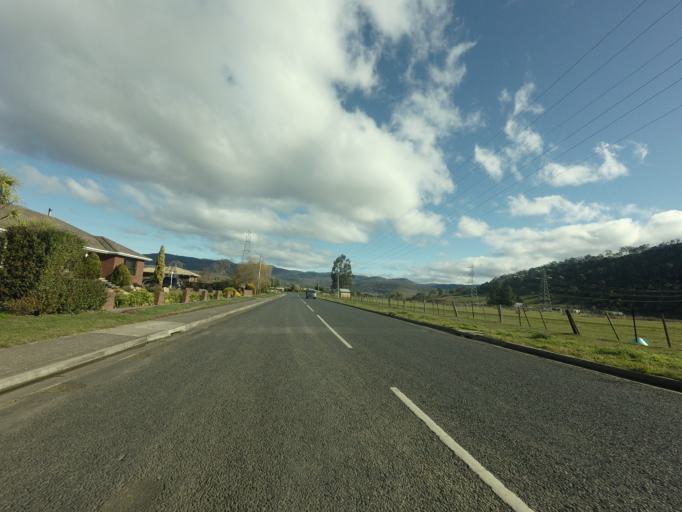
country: AU
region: Tasmania
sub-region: Derwent Valley
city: New Norfolk
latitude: -42.7579
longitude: 147.0486
